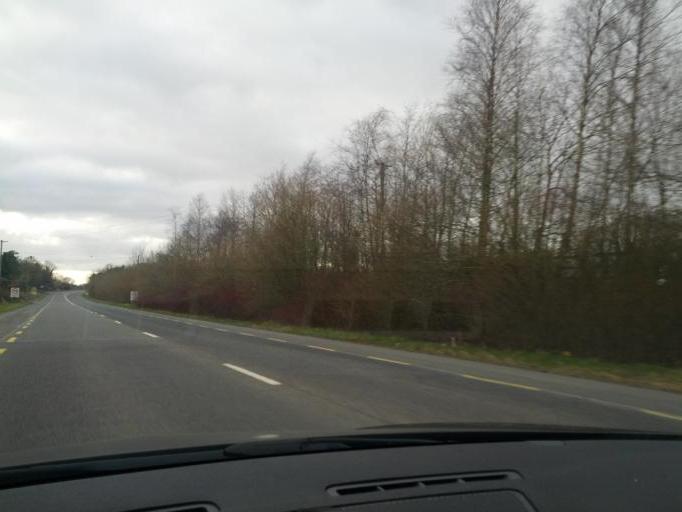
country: IE
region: Leinster
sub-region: An Iarmhi
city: Moate
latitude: 53.3918
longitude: -7.8043
